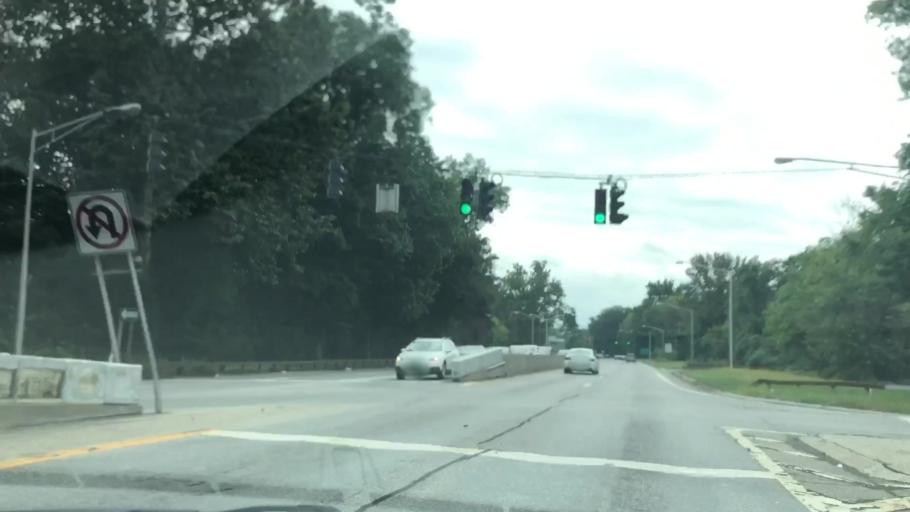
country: US
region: New York
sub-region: Westchester County
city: Hastings-on-Hudson
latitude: 40.9810
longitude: -73.8674
